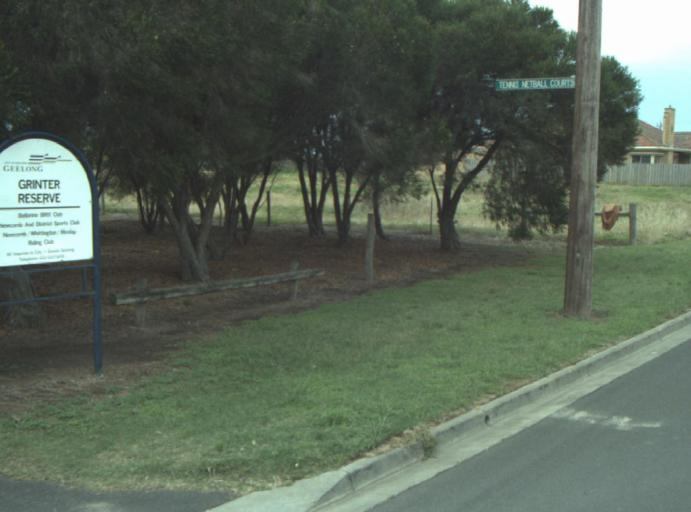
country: AU
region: Victoria
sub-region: Greater Geelong
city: Breakwater
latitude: -38.1807
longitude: 144.4012
